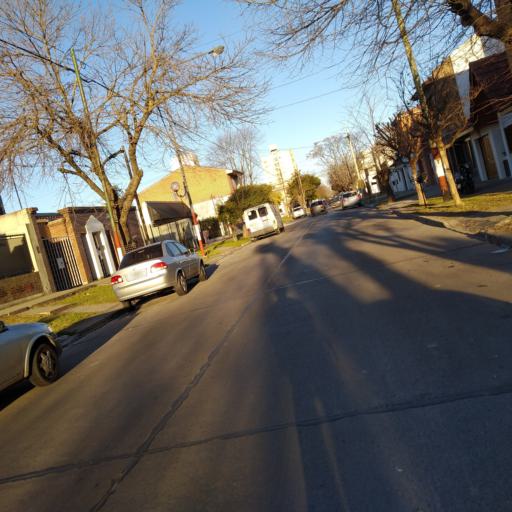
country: AR
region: Buenos Aires
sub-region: Partido de La Plata
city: La Plata
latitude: -34.9290
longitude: -57.9810
